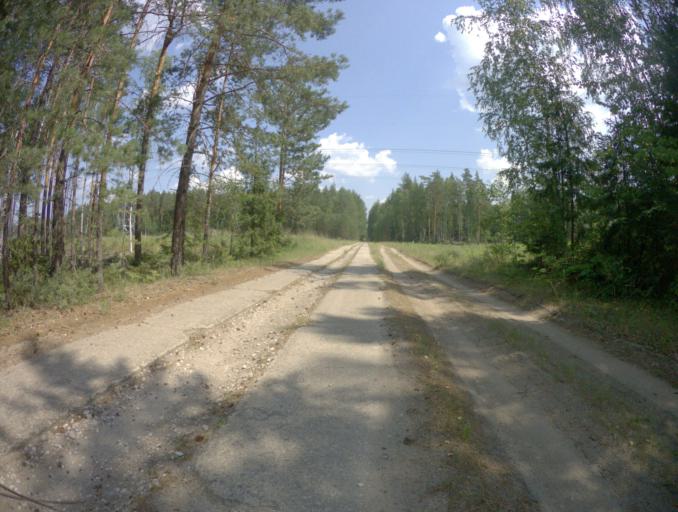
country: RU
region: Nizjnij Novgorod
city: Frolishchi
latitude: 56.4327
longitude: 42.6112
